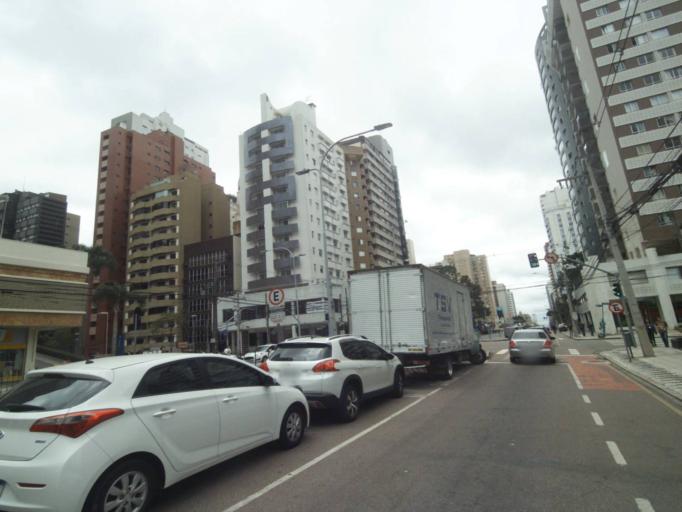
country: BR
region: Parana
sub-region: Curitiba
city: Curitiba
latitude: -25.4439
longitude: -49.2827
